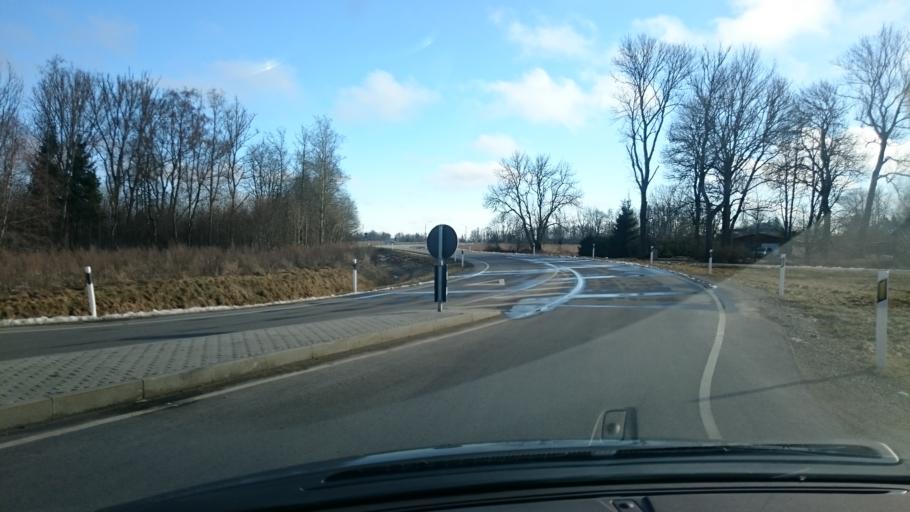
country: EE
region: Harju
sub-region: Kiili vald
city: Kiili
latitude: 59.3463
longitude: 24.8070
